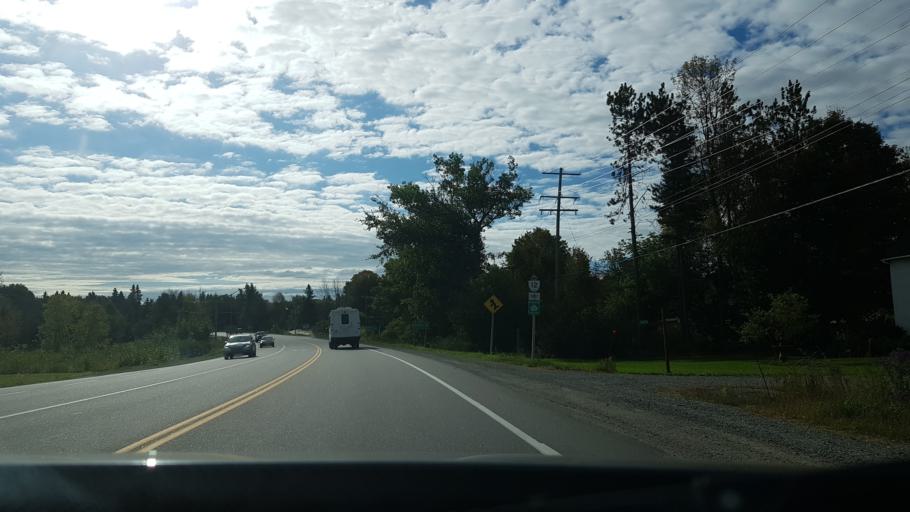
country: CA
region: Ontario
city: Orillia
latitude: 44.6208
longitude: -79.5113
